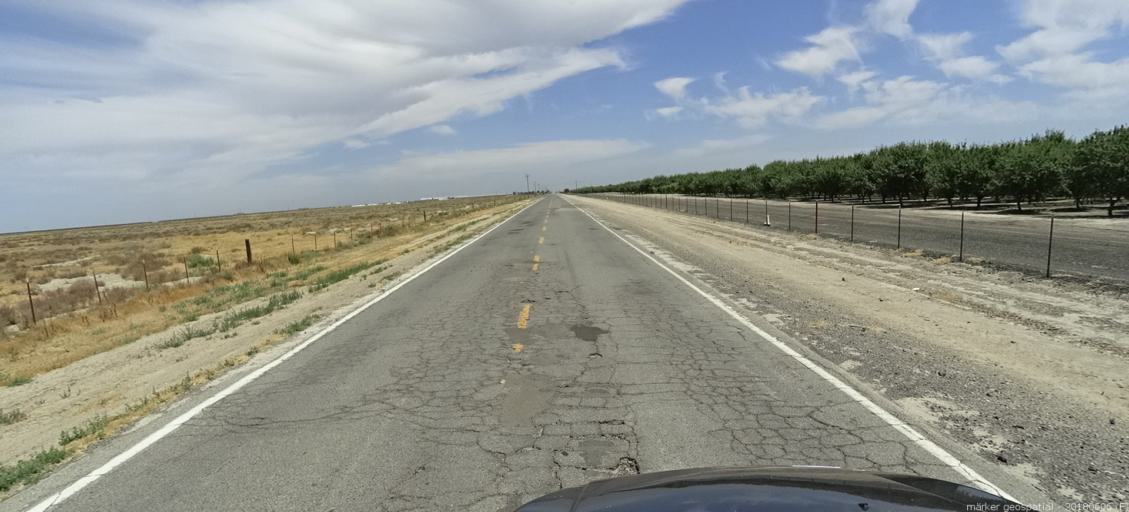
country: US
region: California
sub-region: Fresno County
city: Firebaugh
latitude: 36.9136
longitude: -120.3820
